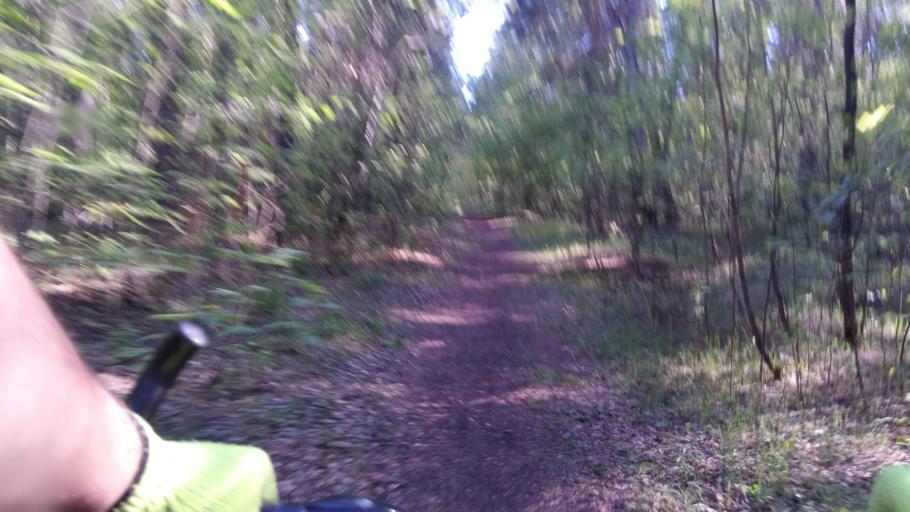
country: RU
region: Chelyabinsk
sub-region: Gorod Chelyabinsk
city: Chelyabinsk
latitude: 55.1504
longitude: 61.3470
